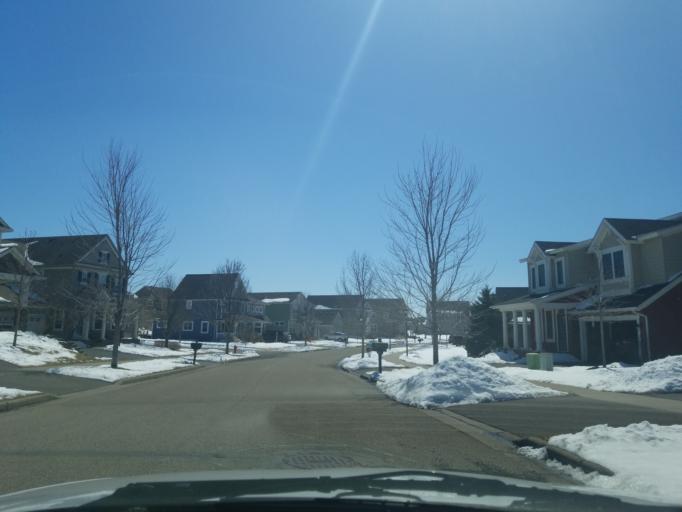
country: US
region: Wisconsin
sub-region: Saint Croix County
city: Hudson
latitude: 44.9549
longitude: -92.7001
